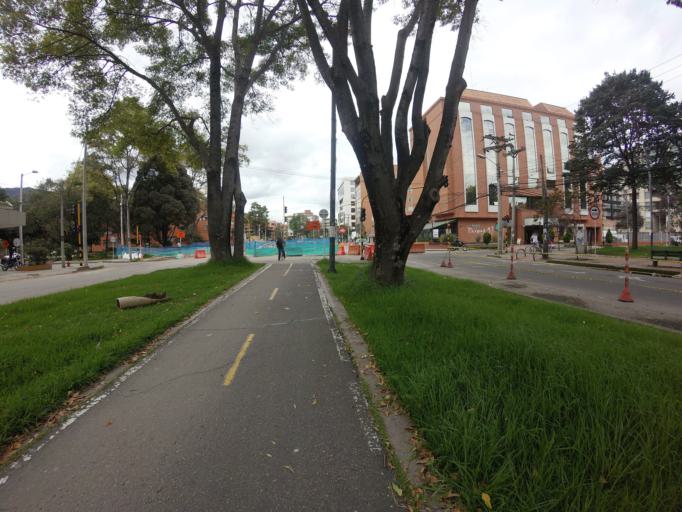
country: CO
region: Bogota D.C.
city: Barrio San Luis
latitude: 4.6843
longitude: -74.0523
